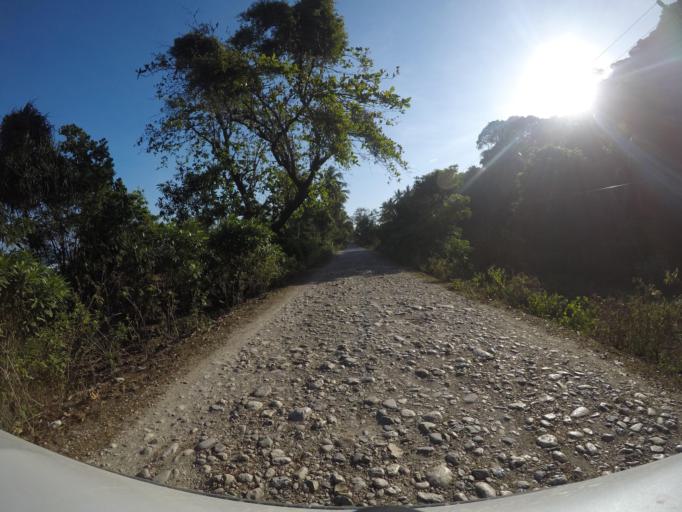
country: TL
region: Viqueque
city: Viqueque
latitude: -8.8000
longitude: 126.5885
